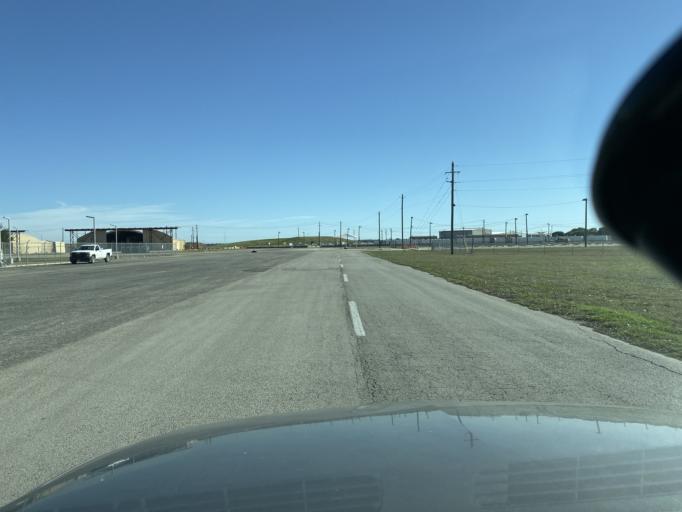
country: US
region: Texas
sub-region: Travis County
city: Hornsby Bend
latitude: 30.1960
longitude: -97.6667
